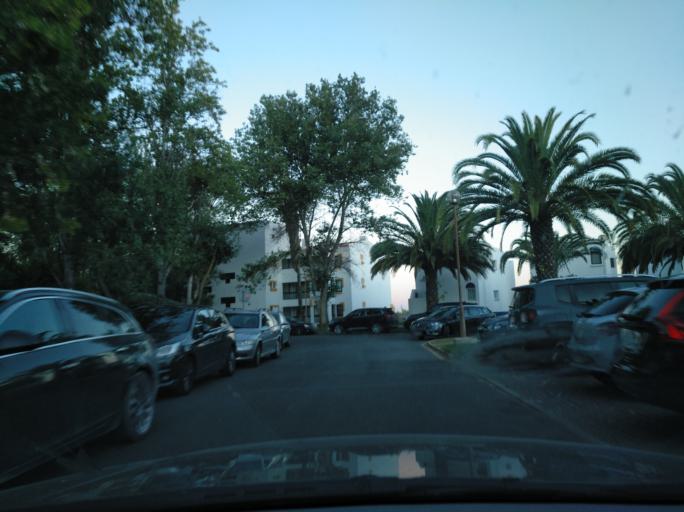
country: PT
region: Faro
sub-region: Tavira
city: Tavira
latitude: 37.1340
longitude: -7.6047
